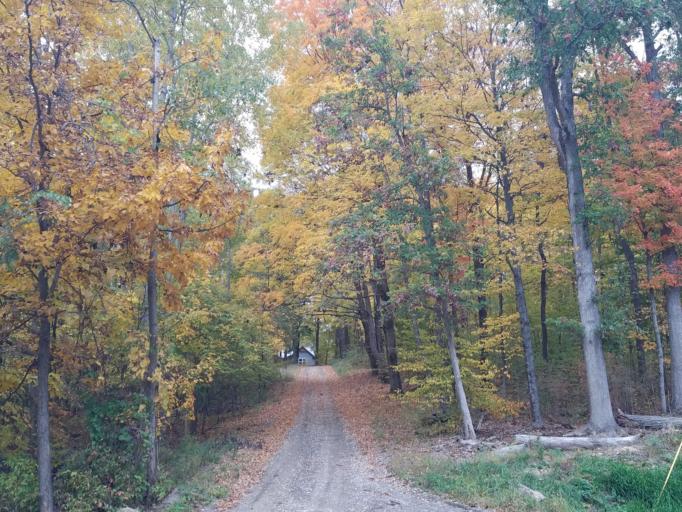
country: US
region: Ohio
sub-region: Sandusky County
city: Bellville
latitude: 40.5692
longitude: -82.3994
